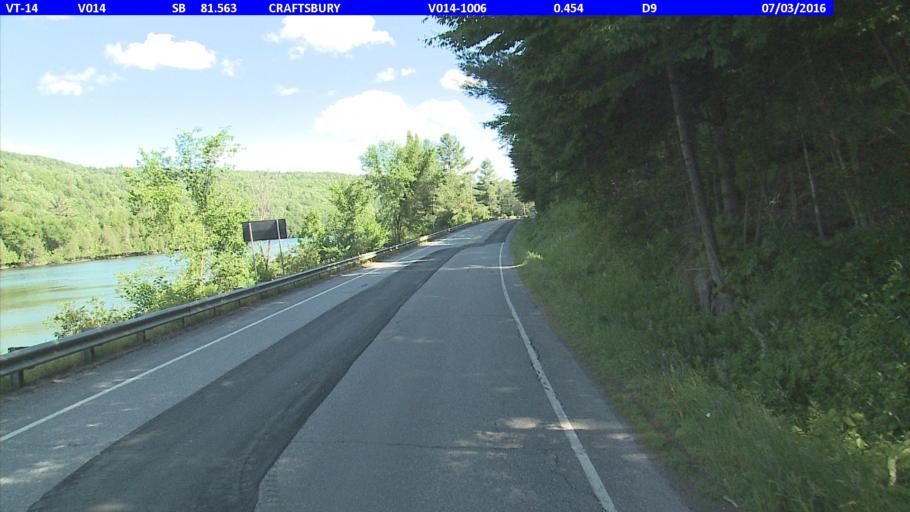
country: US
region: Vermont
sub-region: Caledonia County
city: Hardwick
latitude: 44.6126
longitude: -72.3604
